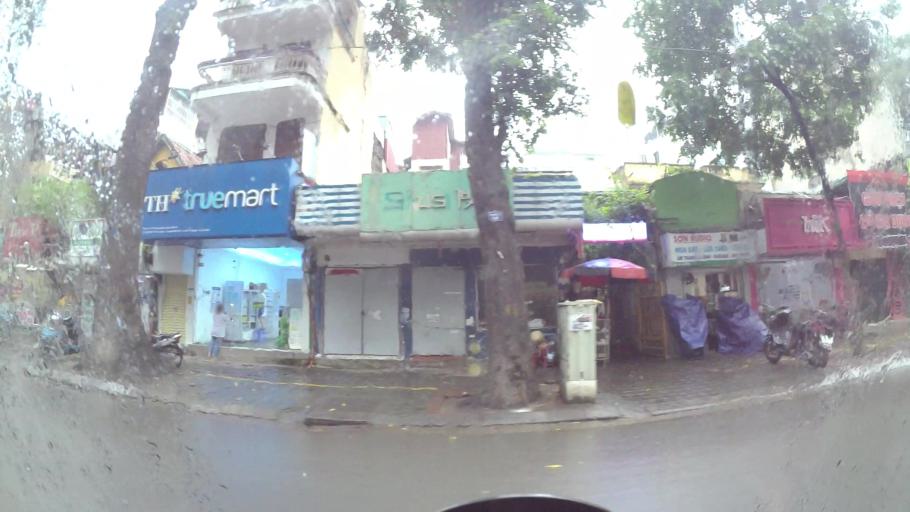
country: VN
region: Ha Noi
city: Hai BaTrung
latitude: 21.0157
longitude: 105.8565
